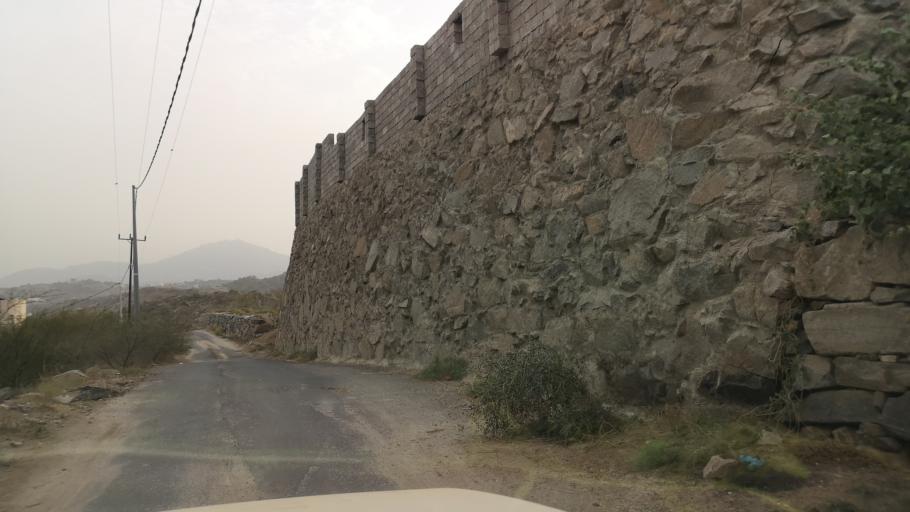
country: YE
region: Sa'dah
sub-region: Monabbih
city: Suq al Khamis
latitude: 17.3738
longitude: 43.1269
